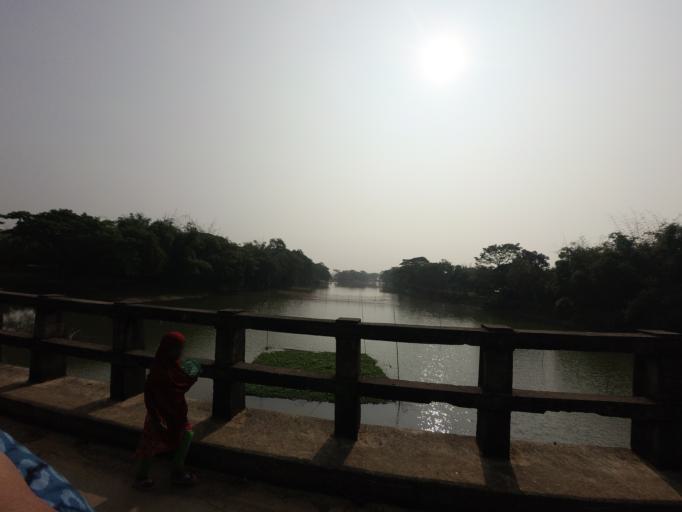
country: BD
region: Dhaka
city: Netrakona
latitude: 25.0095
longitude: 90.6839
